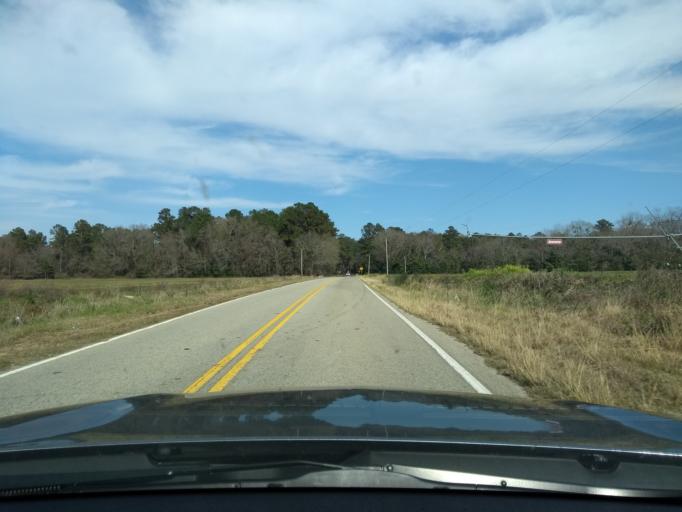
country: US
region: Georgia
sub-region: Bulloch County
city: Brooklet
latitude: 32.4849
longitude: -81.6247
